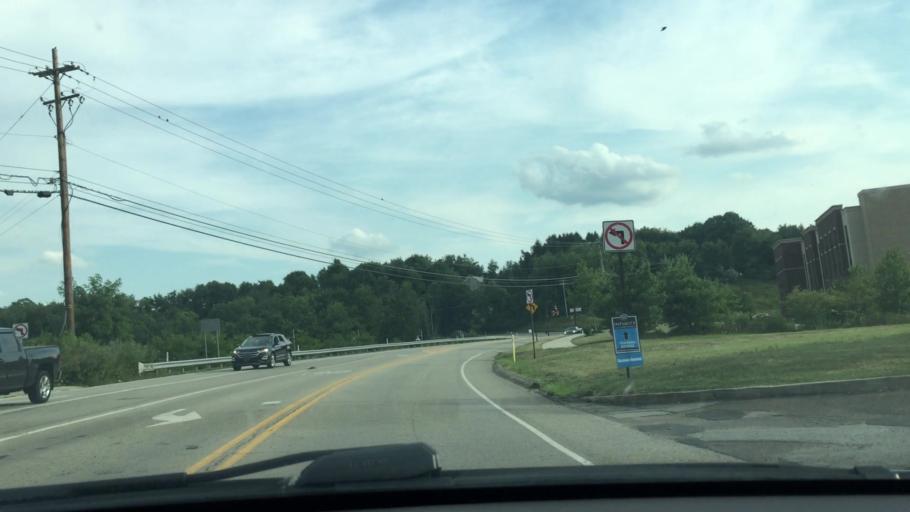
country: US
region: Pennsylvania
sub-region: Butler County
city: Seven Fields
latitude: 40.6850
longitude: -80.0749
